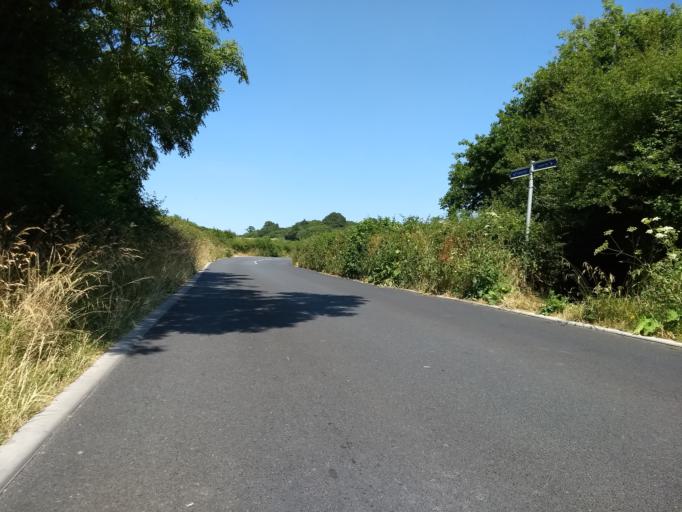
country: GB
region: England
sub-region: Isle of Wight
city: Shalfleet
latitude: 50.7206
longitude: -1.3655
